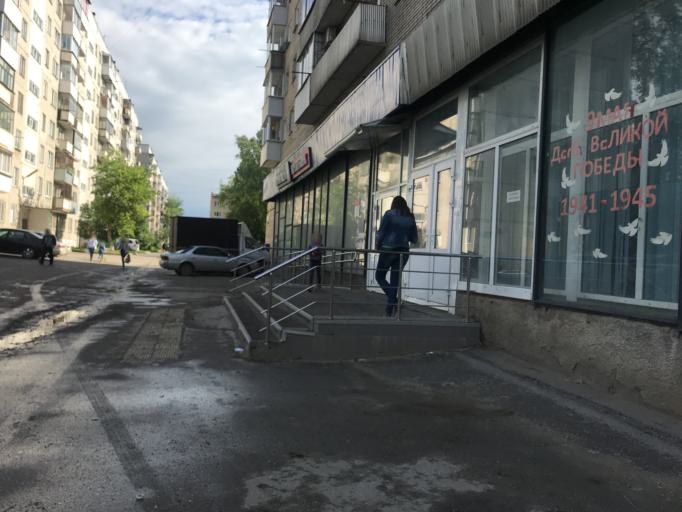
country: RU
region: Novosibirsk
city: Krasnoobsk
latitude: 54.9333
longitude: 82.9071
